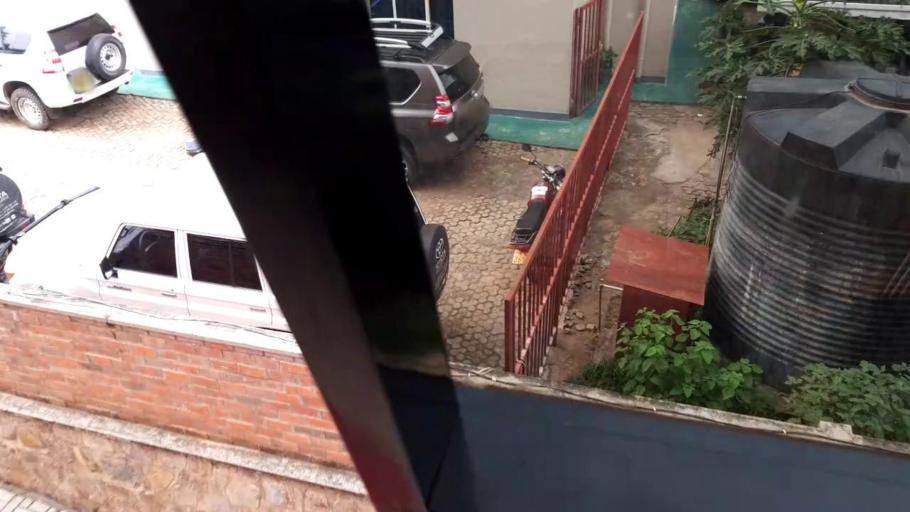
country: RW
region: Kigali
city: Kigali
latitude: -1.9436
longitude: 30.0900
